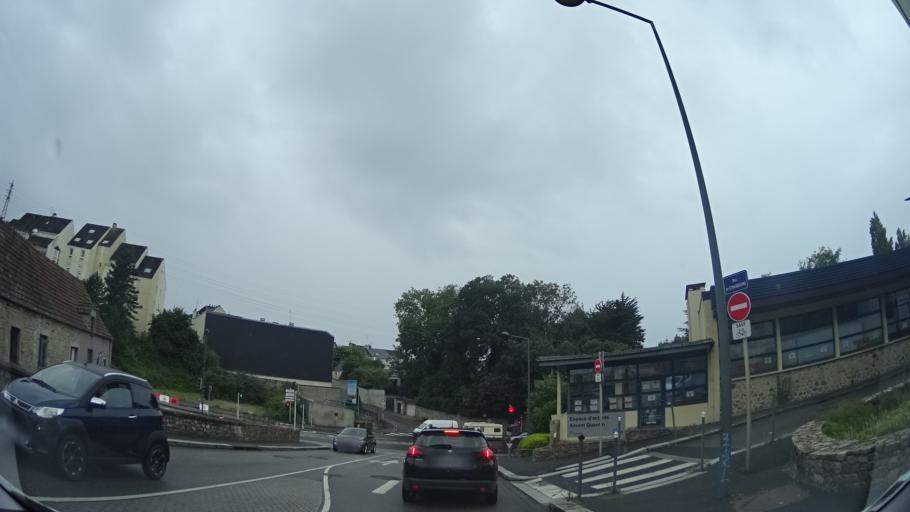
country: FR
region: Lower Normandy
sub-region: Departement de la Manche
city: Cherbourg-Octeville
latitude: 49.6320
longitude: -1.6229
